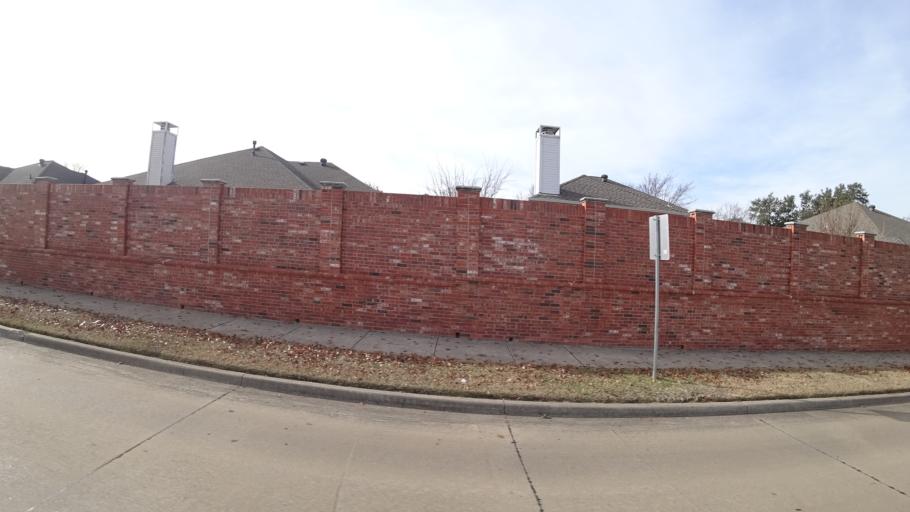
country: US
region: Texas
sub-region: Denton County
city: Highland Village
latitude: 33.0792
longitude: -97.0389
